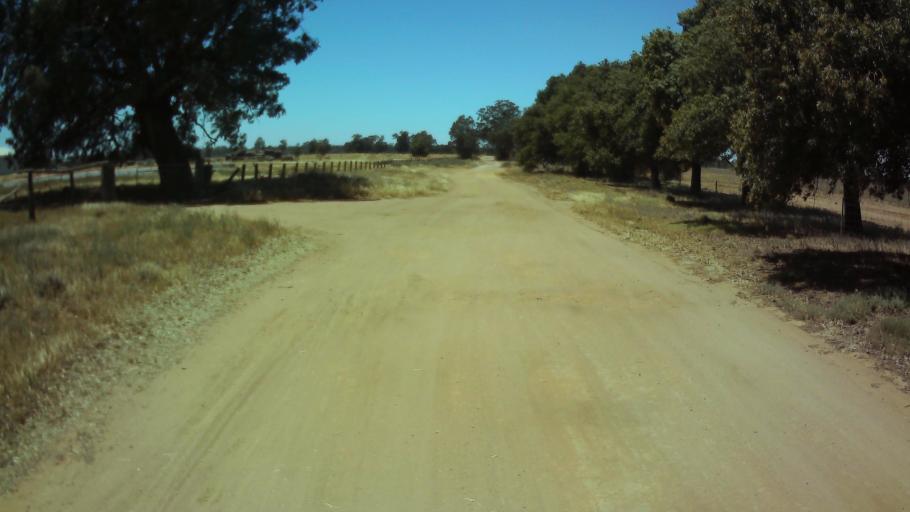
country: AU
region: New South Wales
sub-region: Weddin
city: Grenfell
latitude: -34.0453
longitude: 147.8079
